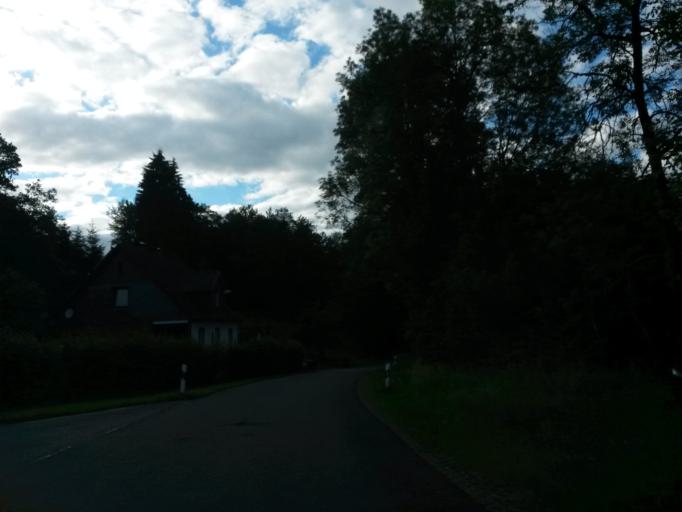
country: DE
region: North Rhine-Westphalia
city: Meinerzhagen
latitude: 51.1054
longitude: 7.7224
